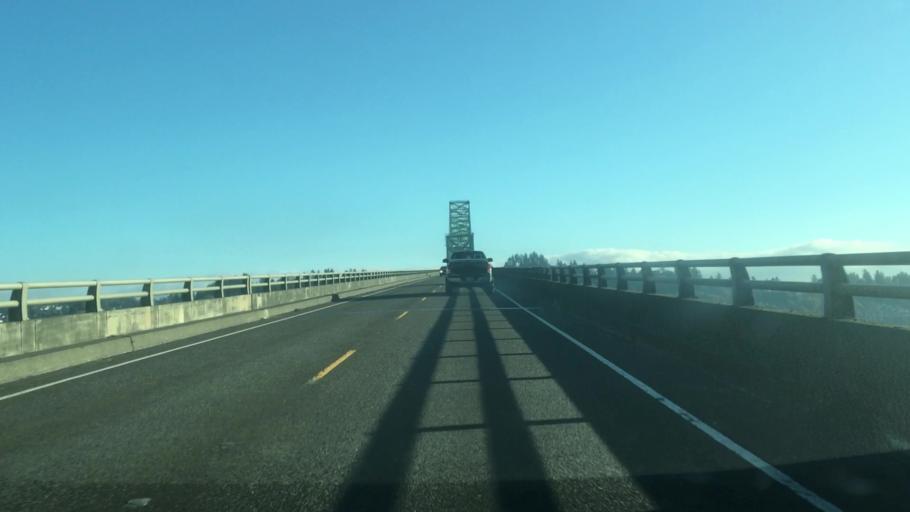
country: US
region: Oregon
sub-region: Clatsop County
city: Astoria
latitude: 46.2006
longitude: -123.8545
